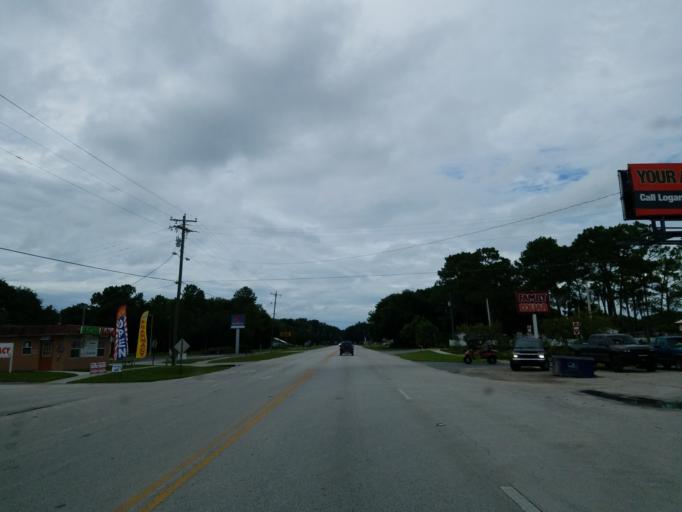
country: US
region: Florida
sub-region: Sumter County
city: Lake Panasoffkee
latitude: 28.7861
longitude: -82.1291
